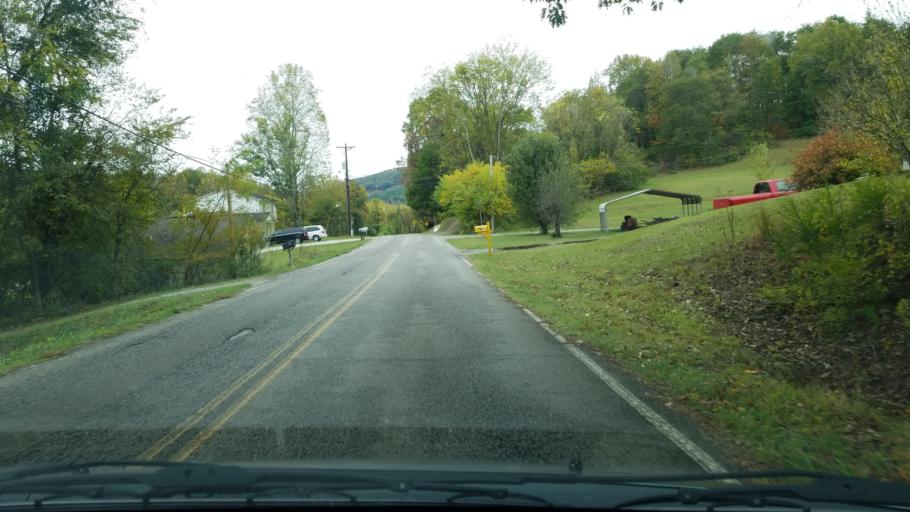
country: US
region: Tennessee
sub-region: Rhea County
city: Dayton
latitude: 35.5151
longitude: -85.0190
